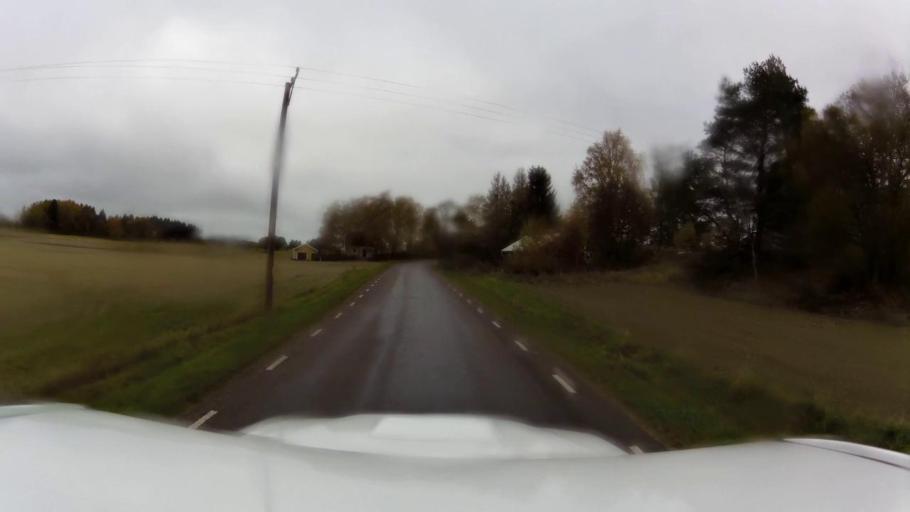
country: SE
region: OEstergoetland
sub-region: Linkopings Kommun
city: Linghem
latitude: 58.4597
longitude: 15.8287
